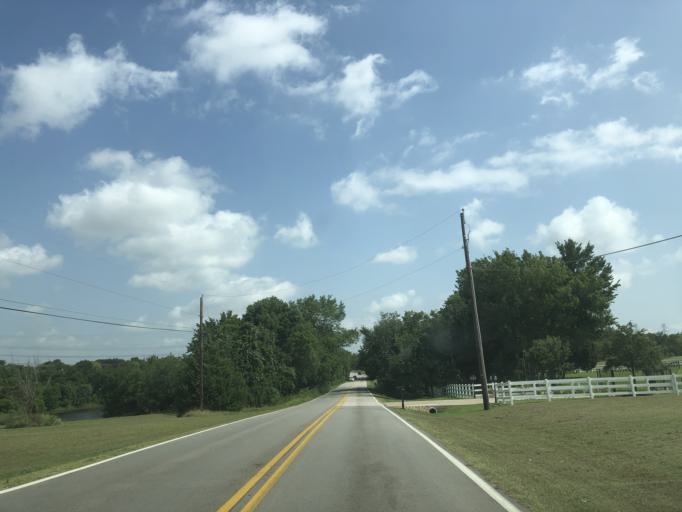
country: US
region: Texas
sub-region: Dallas County
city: Sunnyvale
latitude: 32.8307
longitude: -96.5599
